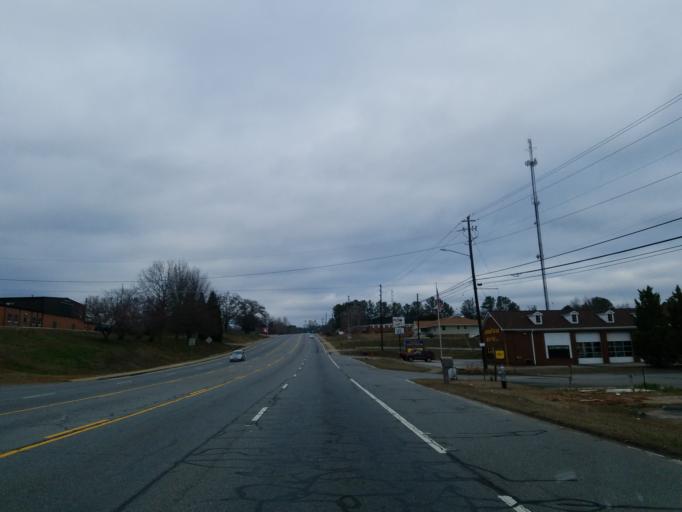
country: US
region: Georgia
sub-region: Cherokee County
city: Canton
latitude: 34.2300
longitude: -84.5000
